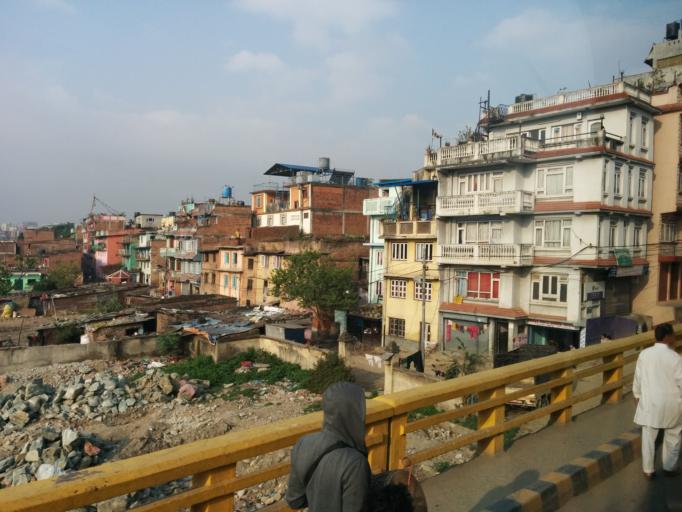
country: NP
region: Central Region
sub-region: Bagmati Zone
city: Kathmandu
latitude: 27.6981
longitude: 85.3021
